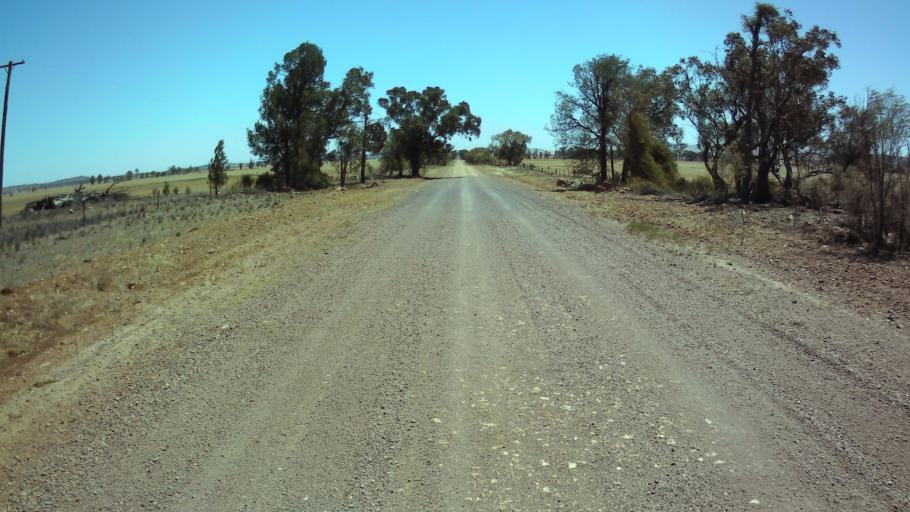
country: AU
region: New South Wales
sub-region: Forbes
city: Forbes
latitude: -33.6908
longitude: 147.7087
